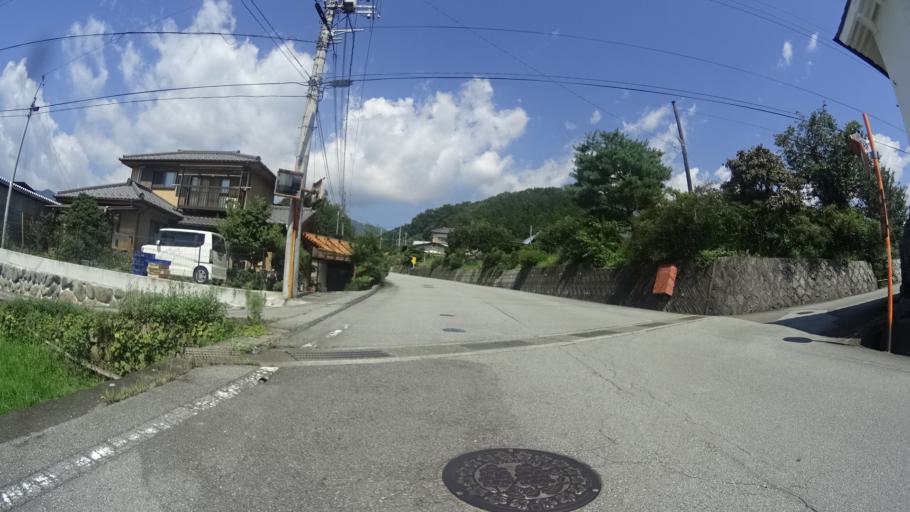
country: JP
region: Yamanashi
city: Enzan
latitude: 35.7507
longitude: 138.7155
